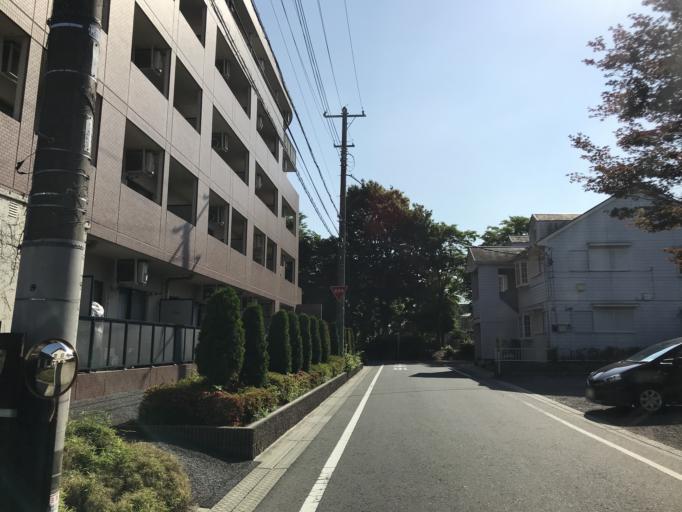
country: JP
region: Ibaraki
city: Naka
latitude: 36.0550
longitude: 140.1329
